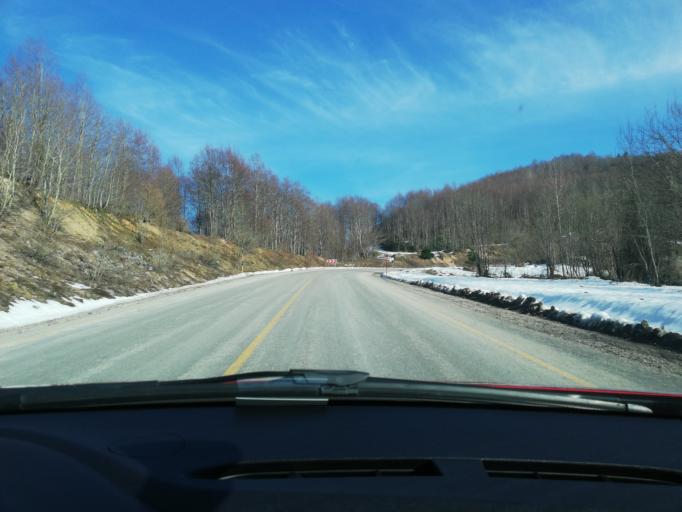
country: TR
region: Kastamonu
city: Cide
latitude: 41.8531
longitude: 33.0663
